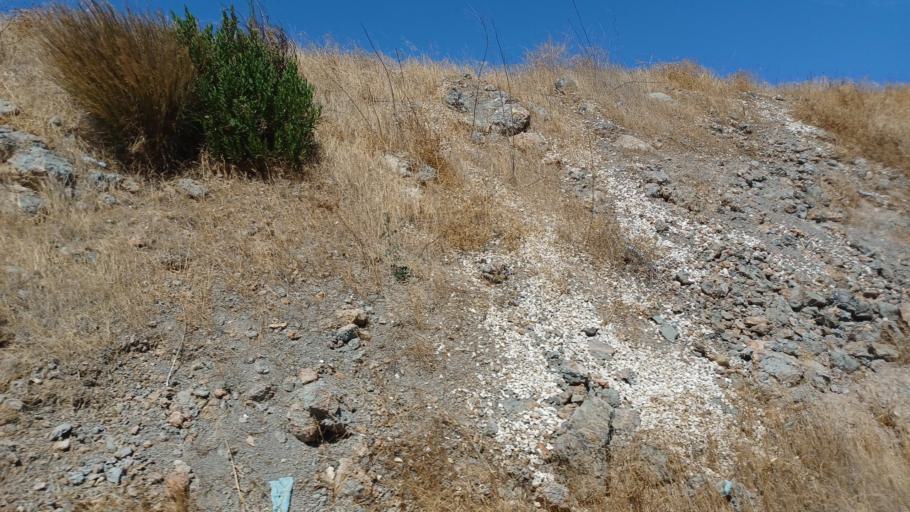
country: CY
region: Larnaka
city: Troulloi
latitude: 35.0240
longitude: 33.5945
